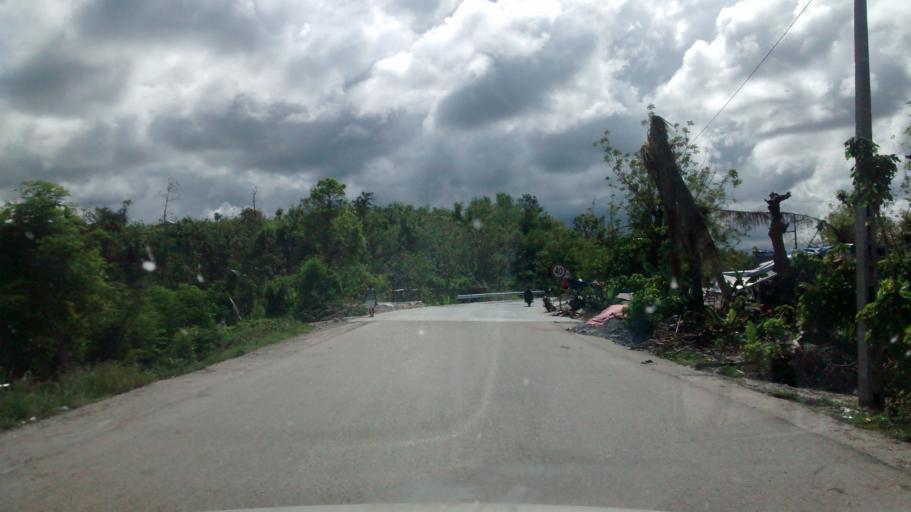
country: HT
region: Grandans
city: Jeremie
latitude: 18.6117
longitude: -74.0763
